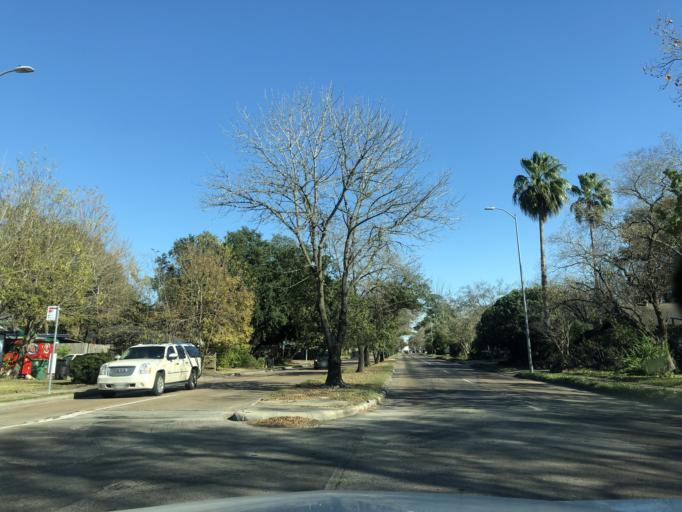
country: US
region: Texas
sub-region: Harris County
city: Bellaire
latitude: 29.6882
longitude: -95.4970
